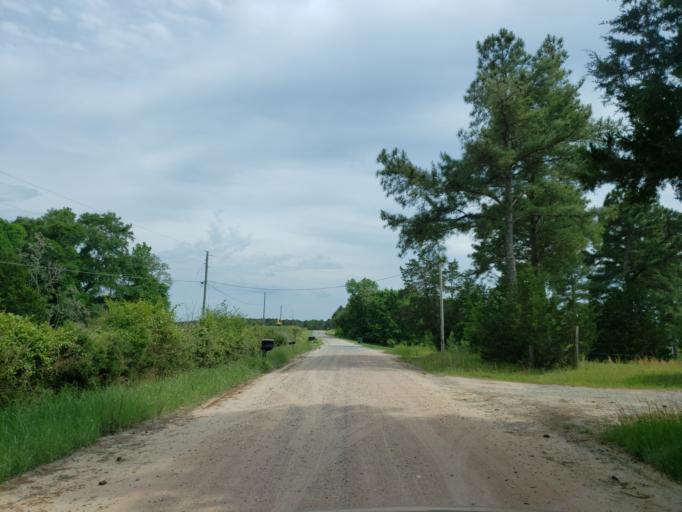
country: US
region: Georgia
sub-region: Monroe County
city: Forsyth
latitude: 32.9680
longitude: -83.9106
